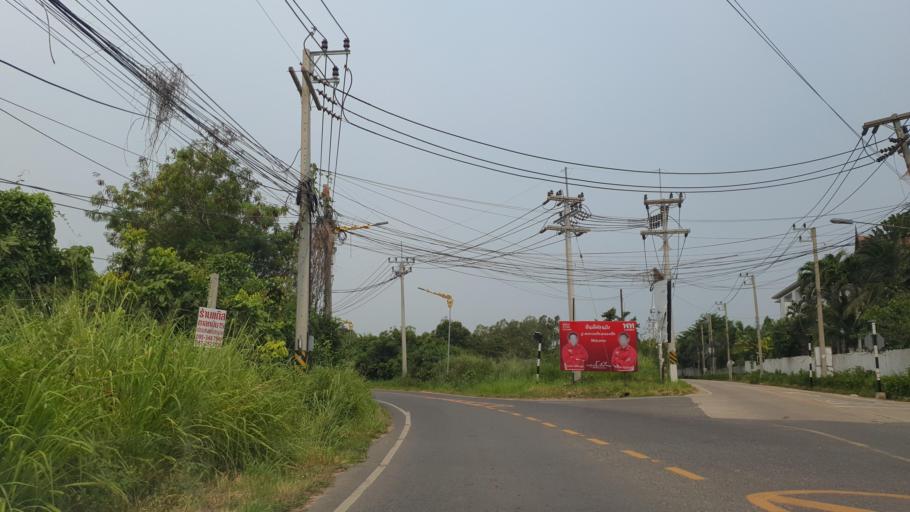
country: TH
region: Chon Buri
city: Phatthaya
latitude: 12.8979
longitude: 100.9157
